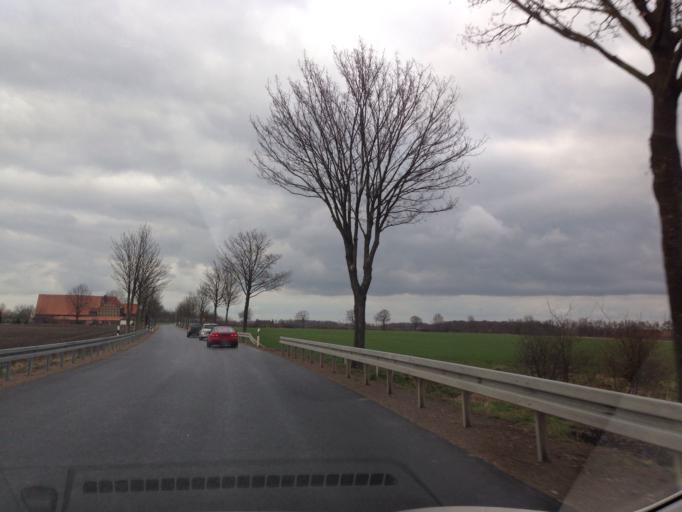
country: DE
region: North Rhine-Westphalia
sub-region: Regierungsbezirk Munster
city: Nordkirchen
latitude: 51.7783
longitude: 7.5458
